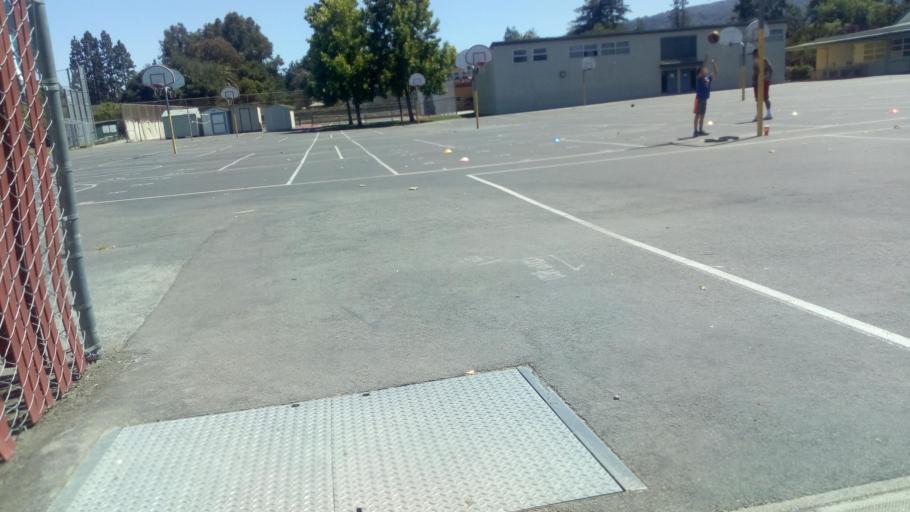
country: US
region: California
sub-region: Santa Clara County
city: Mountain View
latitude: 37.3640
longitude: -122.0821
